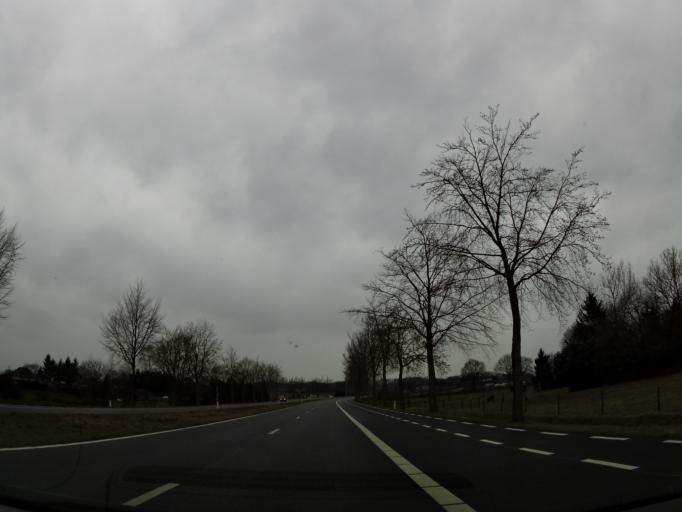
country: BE
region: Flanders
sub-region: Provincie Limburg
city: Maaseik
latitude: 51.0864
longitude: 5.7738
